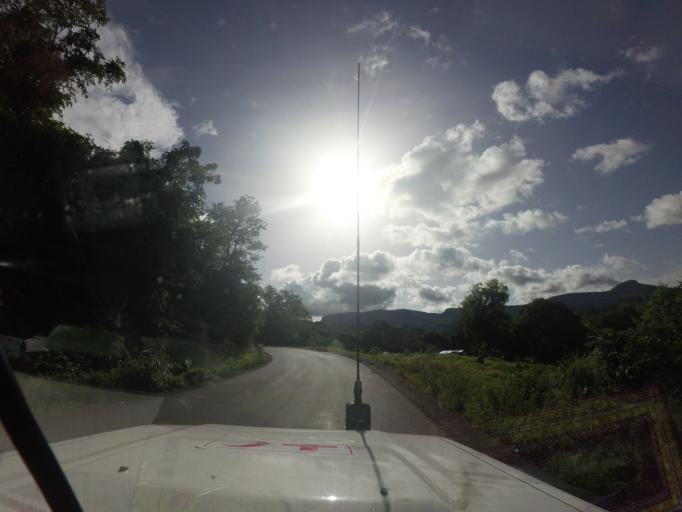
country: GN
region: Kindia
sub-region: Kindia
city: Kindia
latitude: 10.1781
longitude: -12.4785
